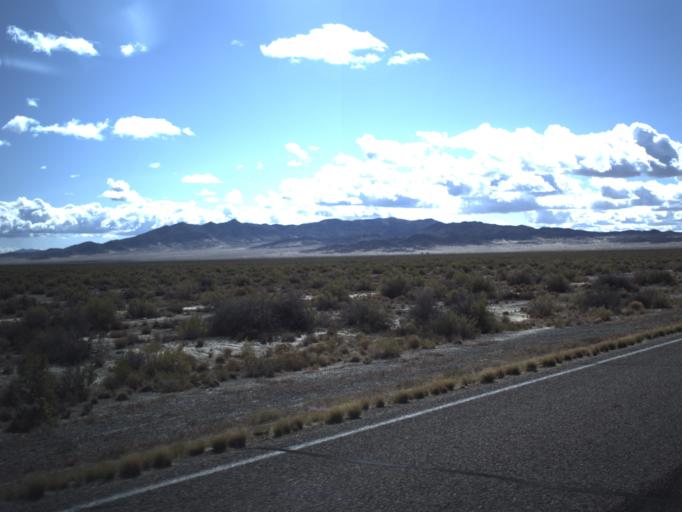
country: US
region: Nevada
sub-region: White Pine County
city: McGill
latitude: 39.0348
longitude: -114.0359
